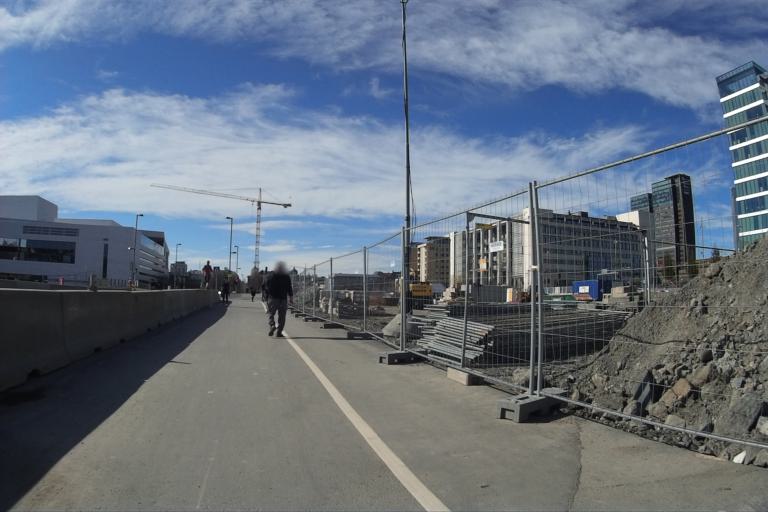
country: NO
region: Oslo
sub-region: Oslo
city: Oslo
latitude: 59.9073
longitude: 10.7567
